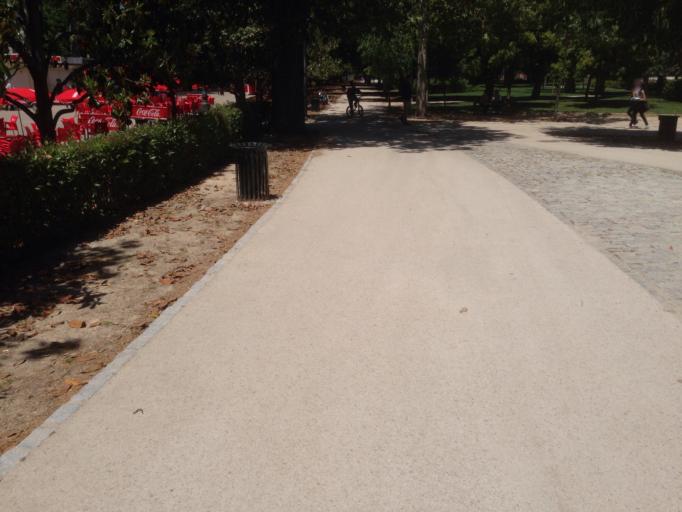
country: ES
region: Madrid
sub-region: Provincia de Madrid
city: Retiro
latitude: 40.4193
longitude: -3.6805
